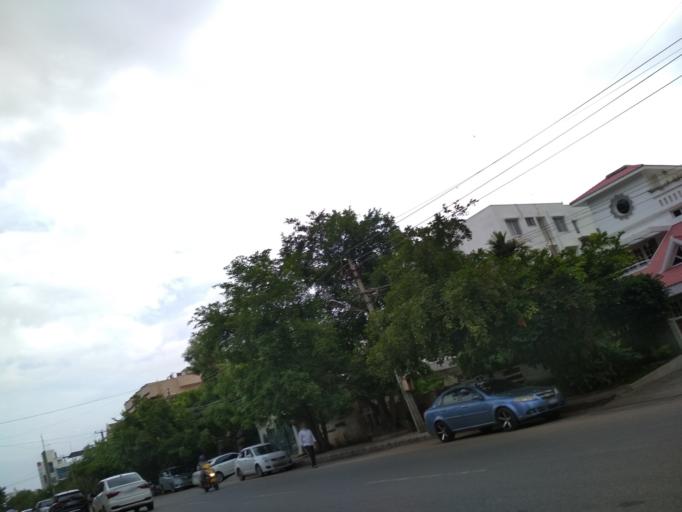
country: IN
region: Karnataka
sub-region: Bangalore Urban
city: Bangalore
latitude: 12.9188
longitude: 77.6450
